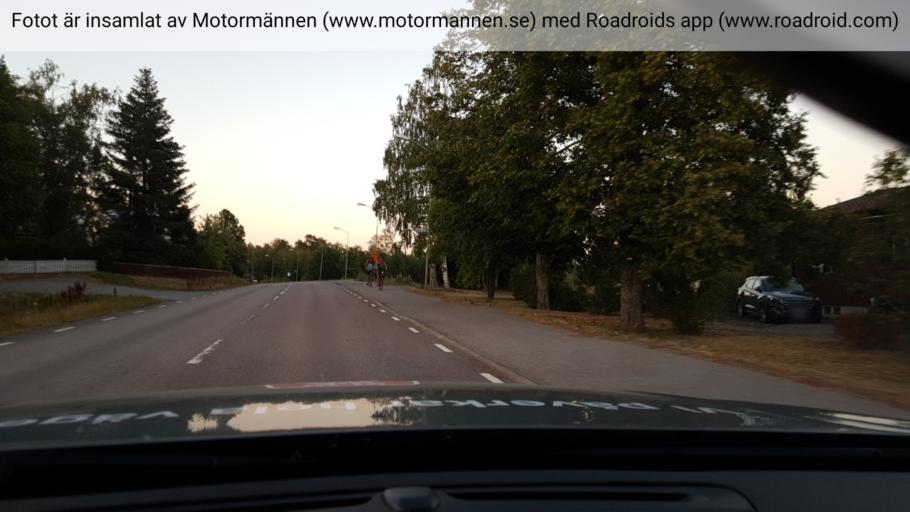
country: SE
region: Uppsala
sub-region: Heby Kommun
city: OEstervala
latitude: 60.1063
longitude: 17.2025
